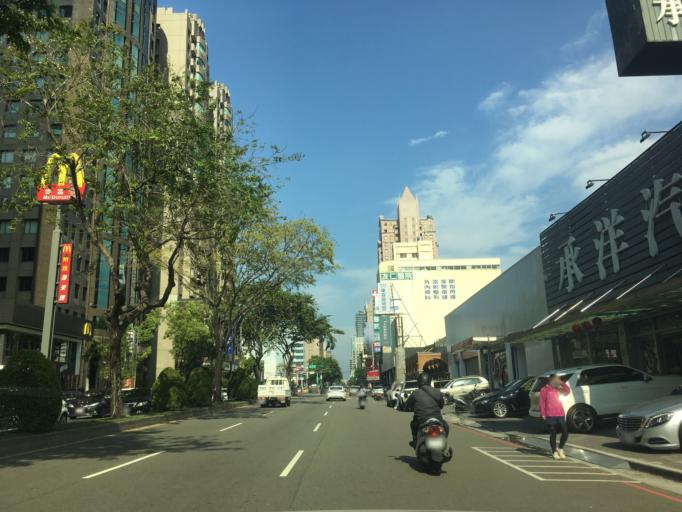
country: TW
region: Taiwan
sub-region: Taichung City
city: Taichung
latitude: 24.1400
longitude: 120.6484
